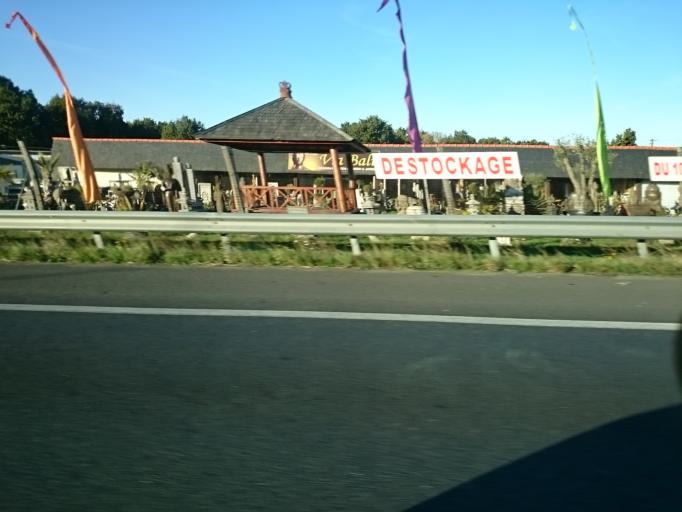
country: FR
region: Brittany
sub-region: Departement des Cotes-d'Armor
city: Coetmieux
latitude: 48.4754
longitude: -2.5767
